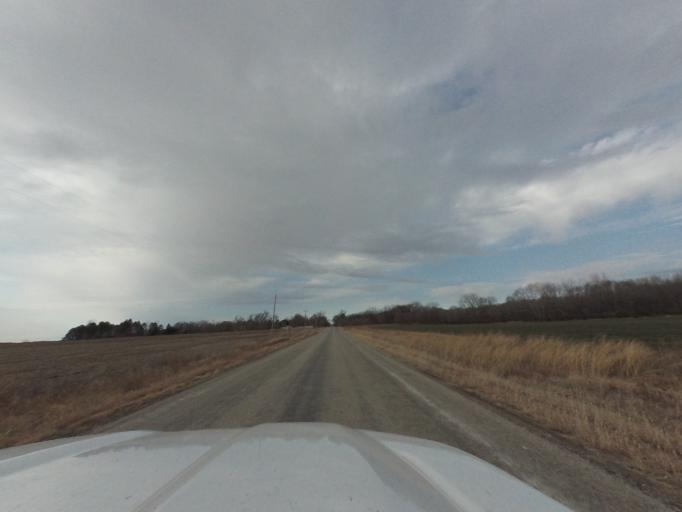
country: US
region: Kansas
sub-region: Chase County
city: Cottonwood Falls
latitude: 38.3735
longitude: -96.6400
